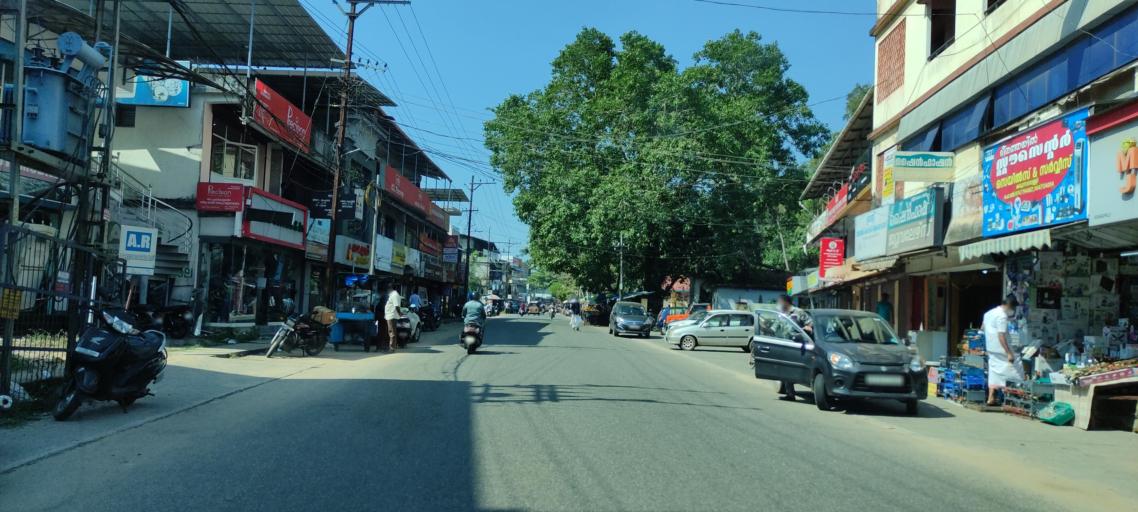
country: IN
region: Kerala
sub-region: Kollam
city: Panmana
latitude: 9.0558
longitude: 76.5378
